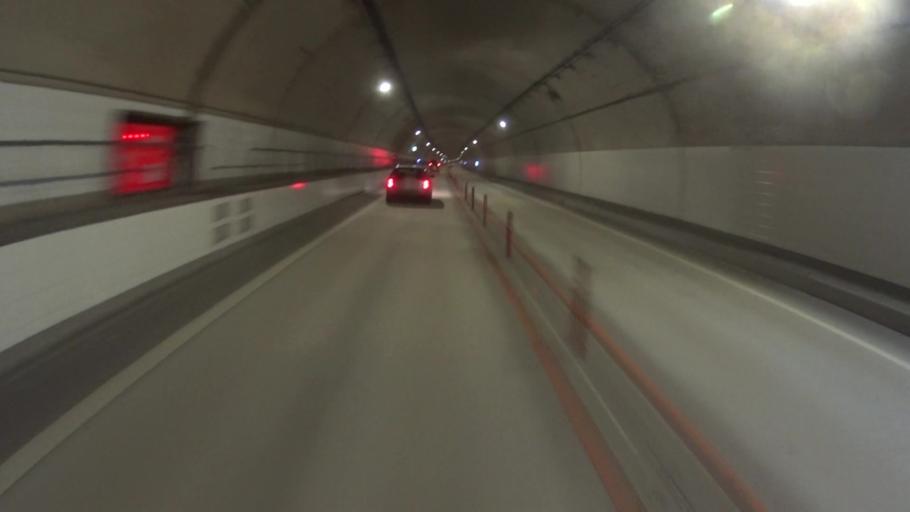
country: JP
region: Kyoto
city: Miyazu
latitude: 35.5365
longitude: 135.1623
